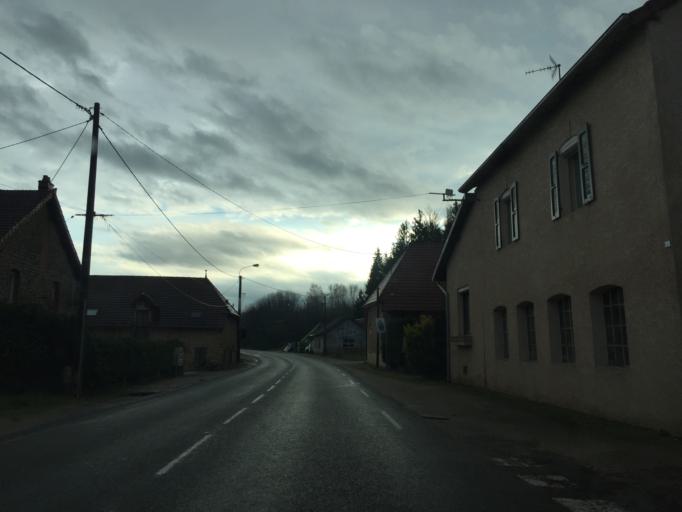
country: FR
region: Franche-Comte
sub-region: Departement du Jura
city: Mont-sous-Vaudrey
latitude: 46.9913
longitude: 5.5591
